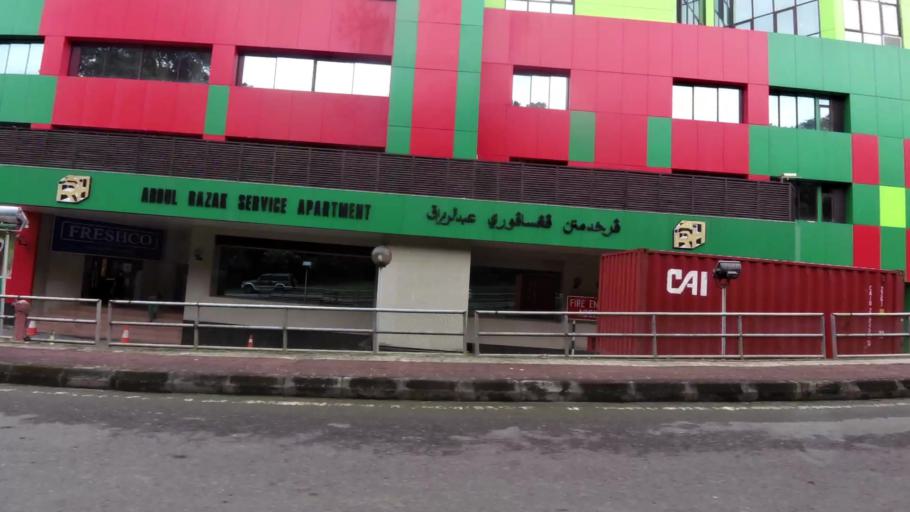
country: BN
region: Brunei and Muara
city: Bandar Seri Begawan
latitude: 4.8853
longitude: 114.9316
